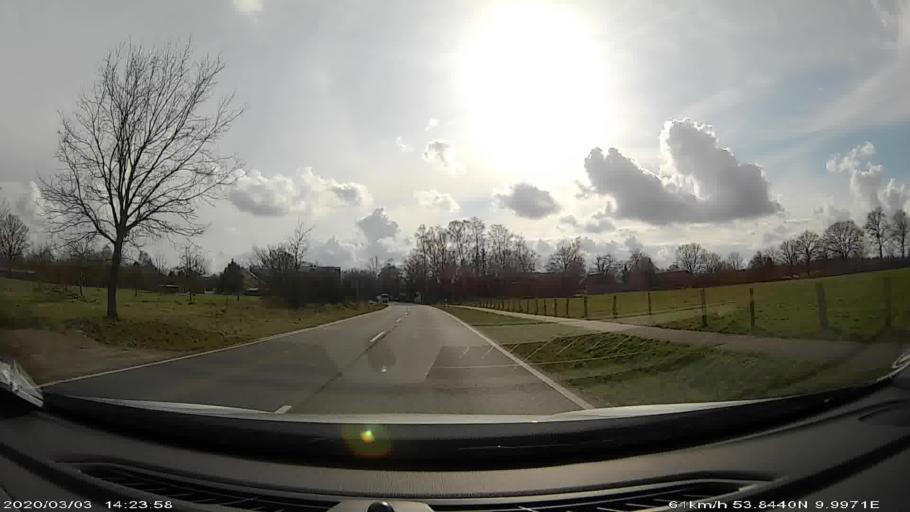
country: DE
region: Schleswig-Holstein
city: Oersdorf
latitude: 53.8439
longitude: 9.9967
